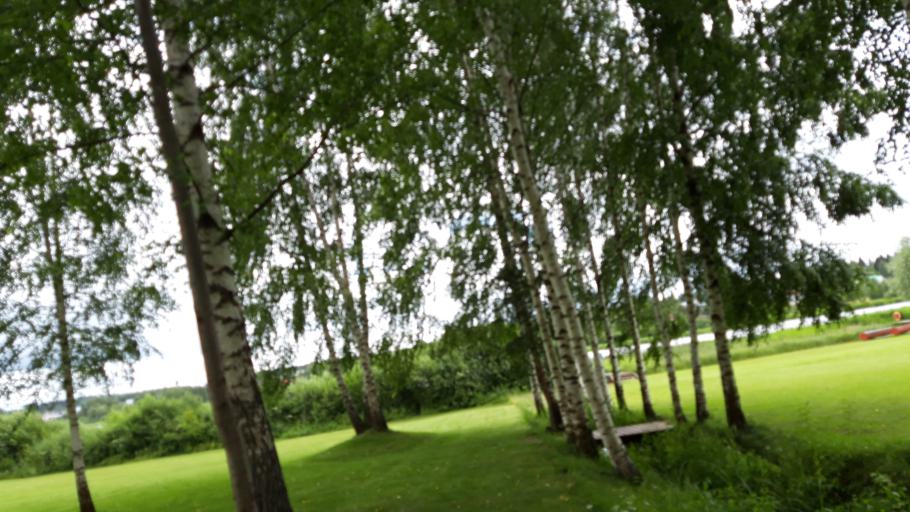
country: RU
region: Tverskaya
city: Konakovo
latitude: 56.6857
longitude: 36.7193
